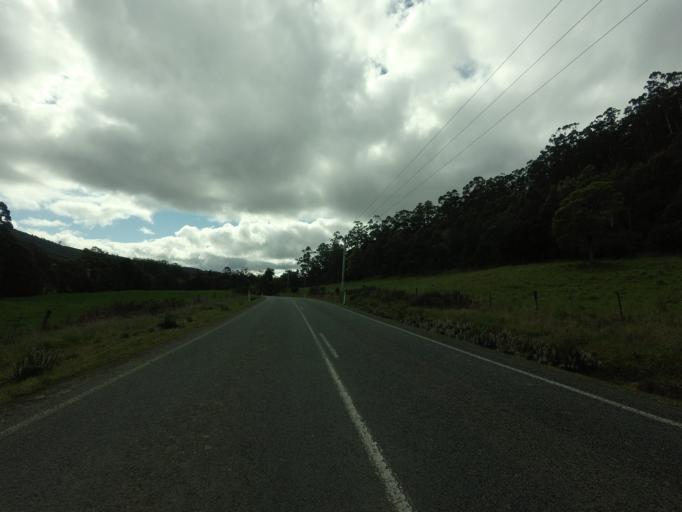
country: AU
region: Tasmania
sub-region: Huon Valley
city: Cygnet
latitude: -43.2811
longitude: 147.0106
